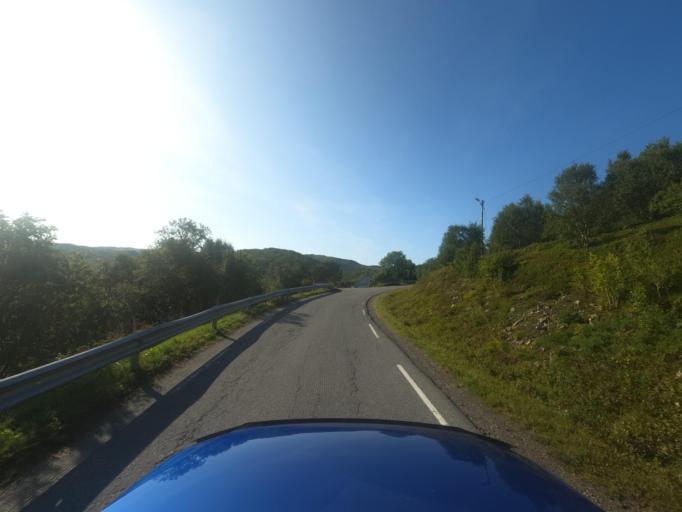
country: NO
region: Nordland
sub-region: Vestvagoy
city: Evjen
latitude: 68.2938
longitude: 13.8659
